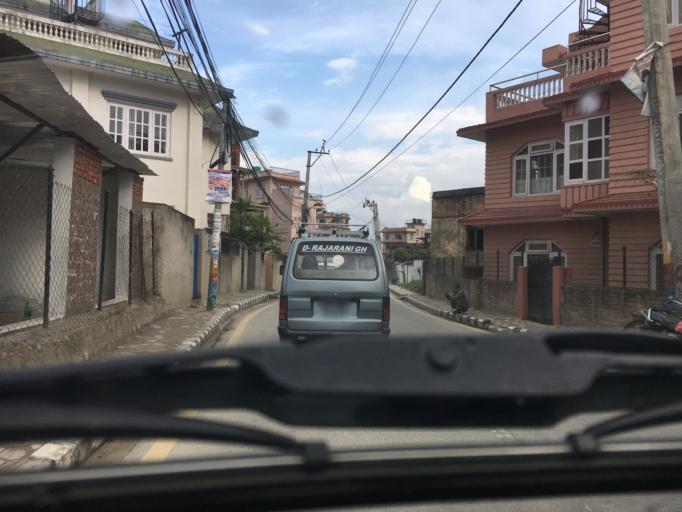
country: NP
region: Central Region
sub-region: Bagmati Zone
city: Kathmandu
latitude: 27.7412
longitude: 85.3483
